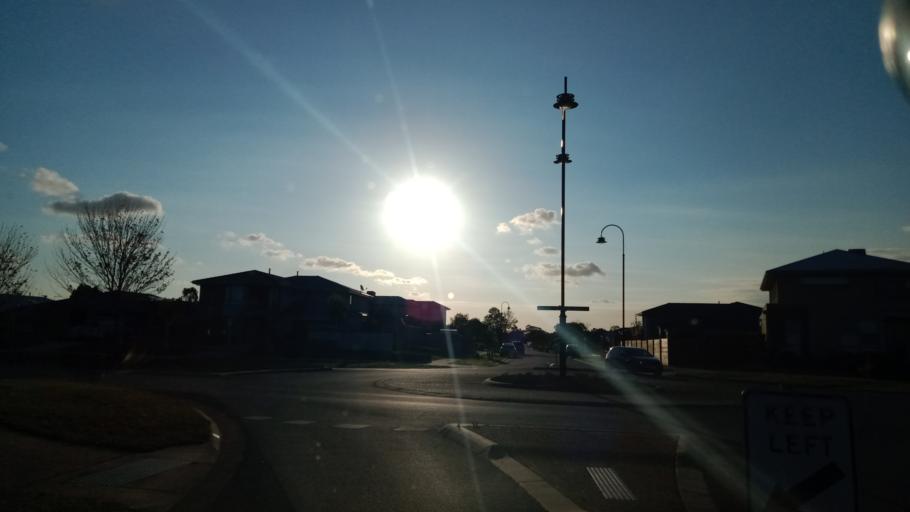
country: AU
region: Victoria
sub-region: Casey
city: Lynbrook
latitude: -38.0753
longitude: 145.2452
